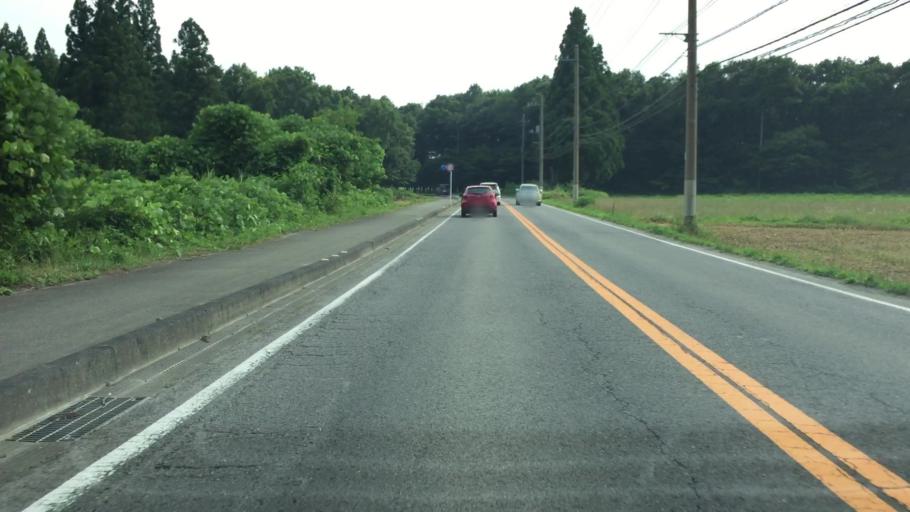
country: JP
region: Tochigi
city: Kuroiso
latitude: 36.9973
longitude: 139.9430
